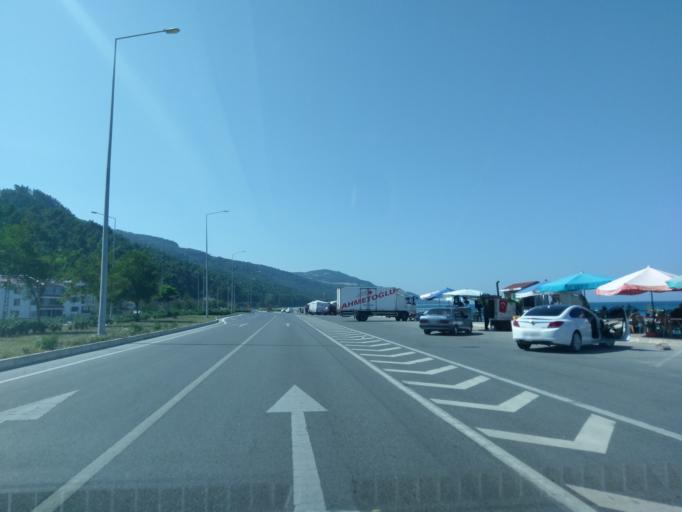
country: TR
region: Samsun
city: Yakakent
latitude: 41.6444
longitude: 35.4799
